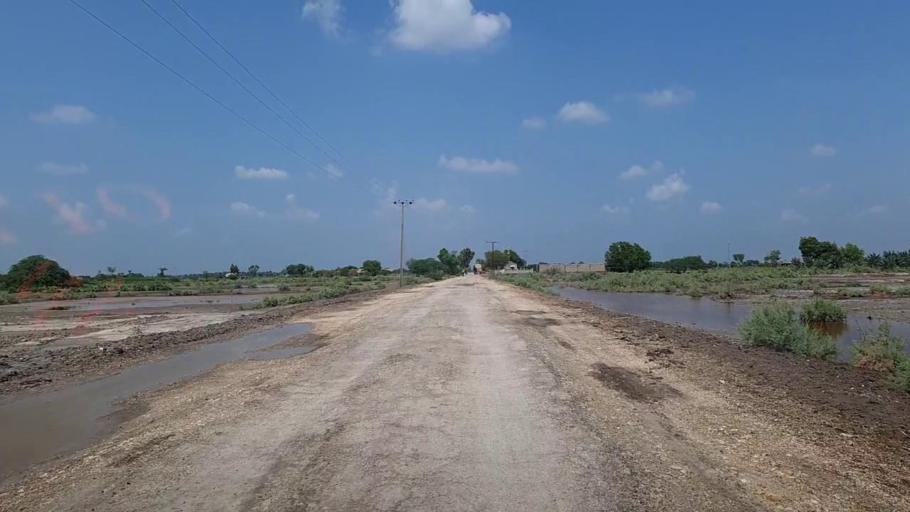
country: PK
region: Sindh
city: Kandiaro
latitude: 27.0069
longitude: 68.2604
